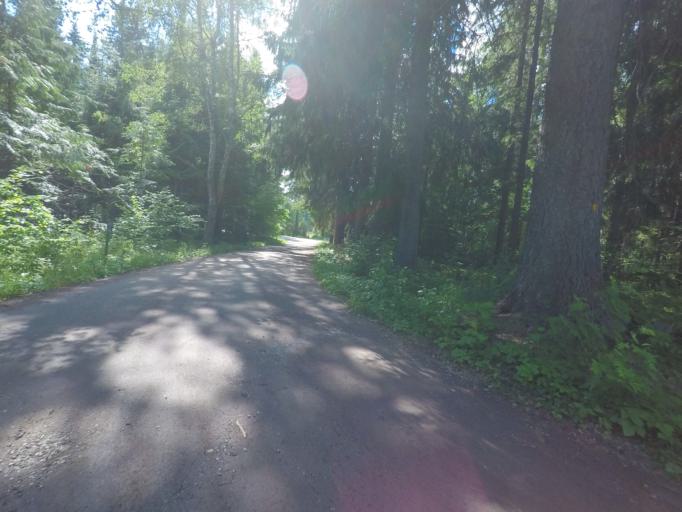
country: FI
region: Southern Savonia
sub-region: Savonlinna
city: Punkaharju
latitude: 61.8039
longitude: 29.3182
